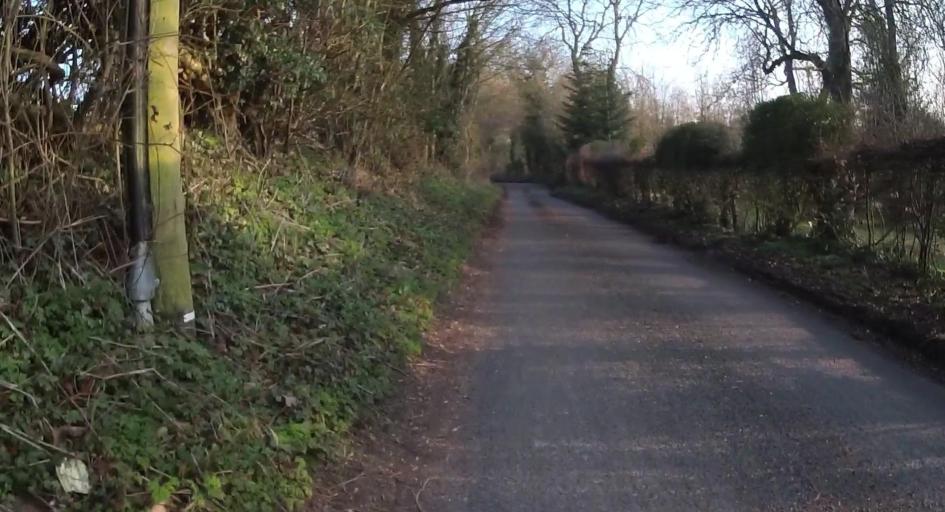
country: GB
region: England
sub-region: Hampshire
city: Alton
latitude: 51.1717
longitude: -1.0026
